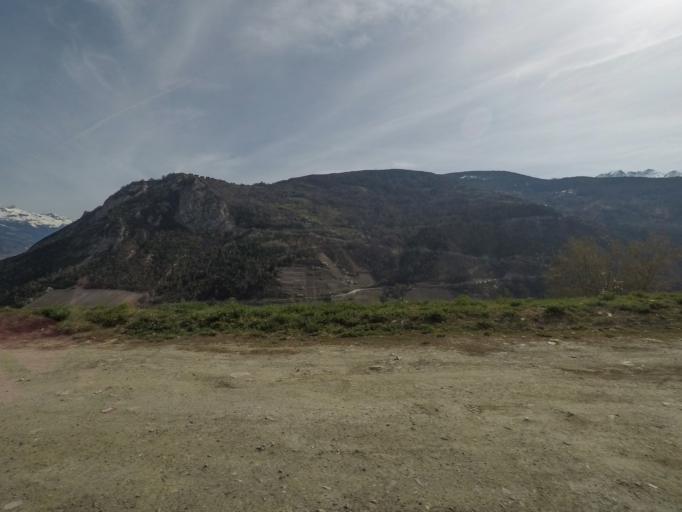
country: CH
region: Valais
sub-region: Herens District
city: Vex
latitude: 46.2183
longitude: 7.4033
